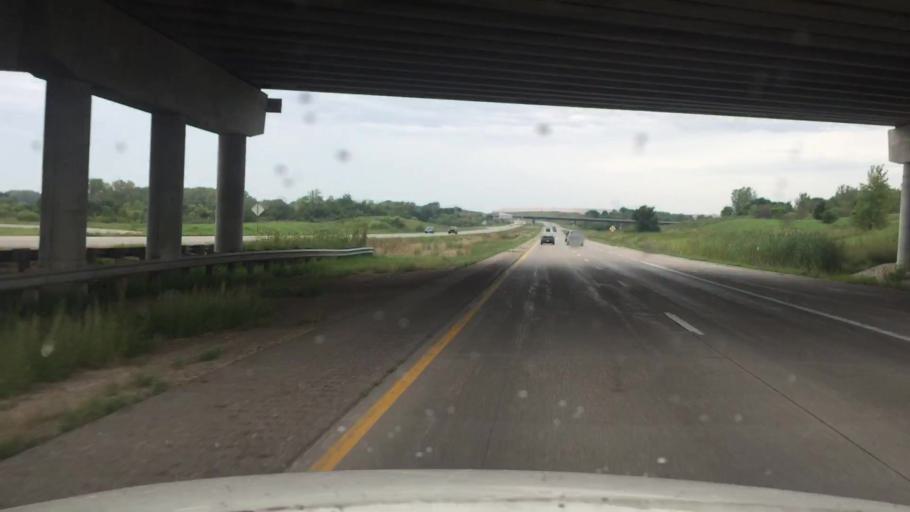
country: US
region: Iowa
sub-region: Warren County
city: Norwalk
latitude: 41.5077
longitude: -93.6449
